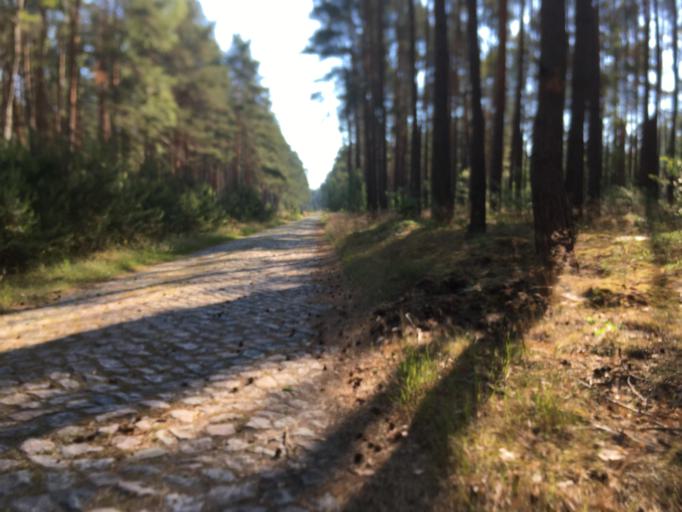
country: DE
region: Brandenburg
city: Marienwerder
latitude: 52.9443
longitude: 13.6352
